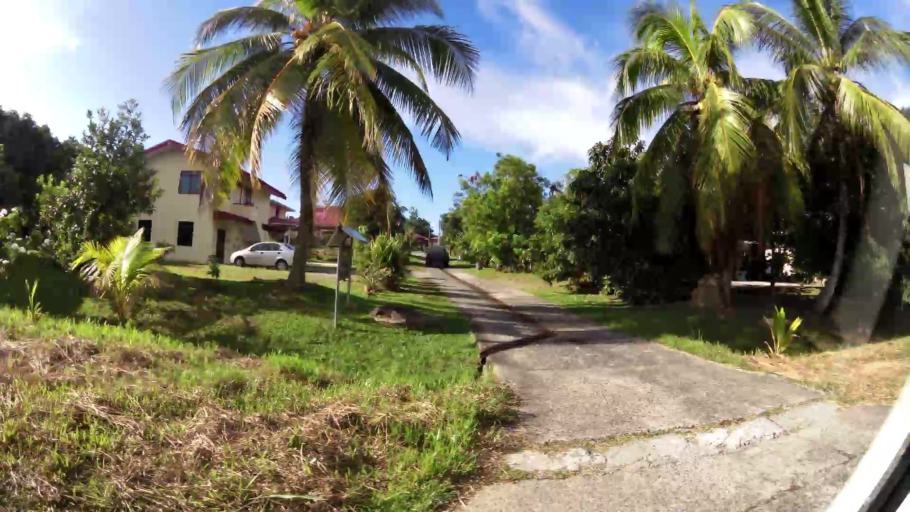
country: BN
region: Brunei and Muara
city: Bandar Seri Begawan
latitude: 4.9779
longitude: 114.9660
